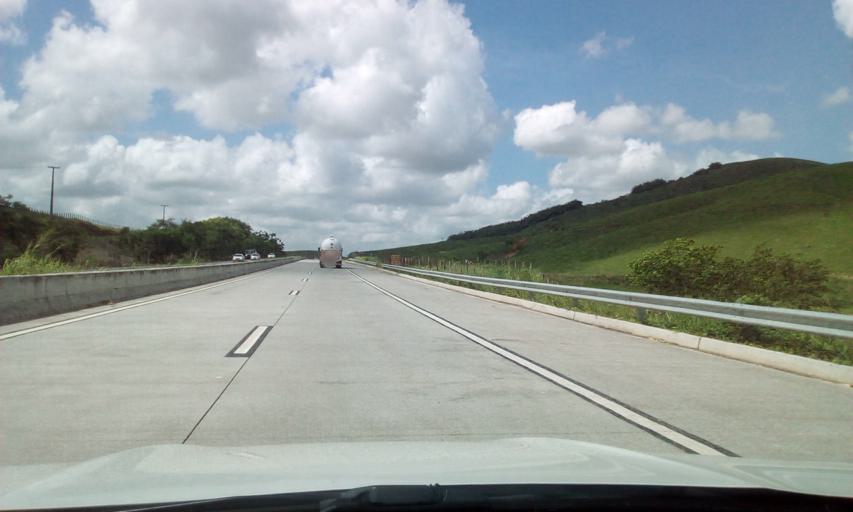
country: BR
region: Alagoas
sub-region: Flexeiras
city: Flexeiras
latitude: -9.2582
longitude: -35.7758
